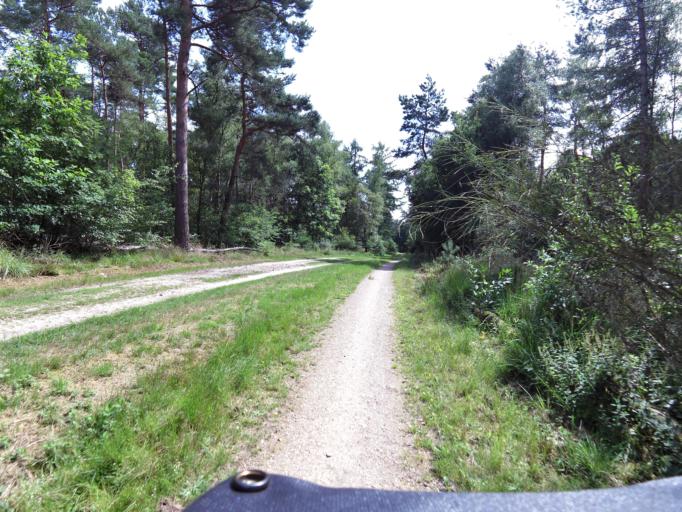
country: NL
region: Limburg
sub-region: Gemeente Roerdalen
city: Vlodrop
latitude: 51.1549
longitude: 6.1075
